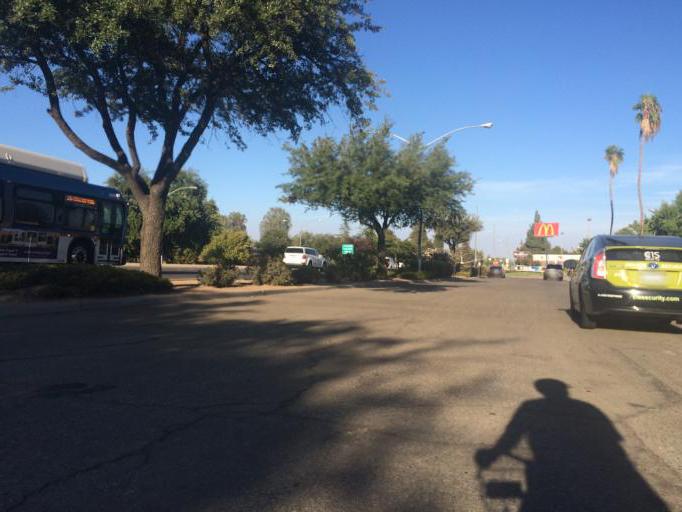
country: US
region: California
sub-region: Fresno County
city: Clovis
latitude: 36.8084
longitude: -119.7584
